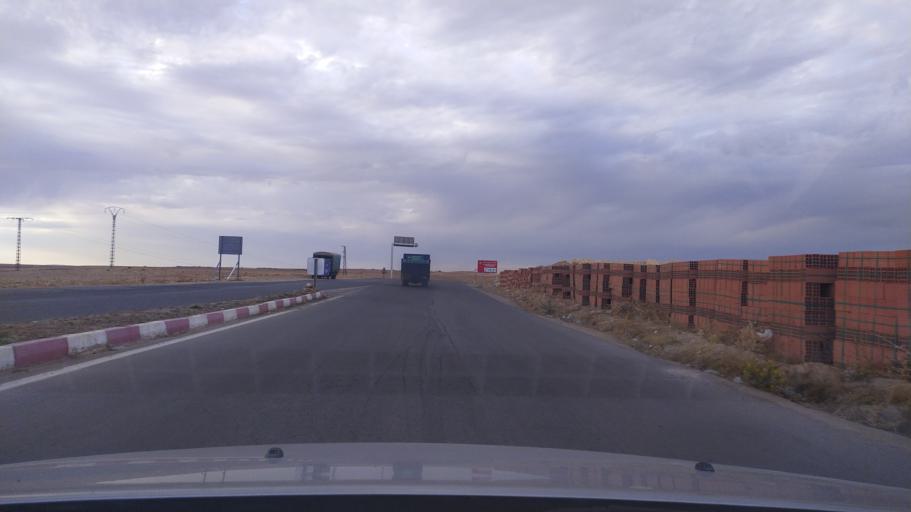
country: DZ
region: Tiaret
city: Frenda
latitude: 34.9926
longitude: 1.1297
